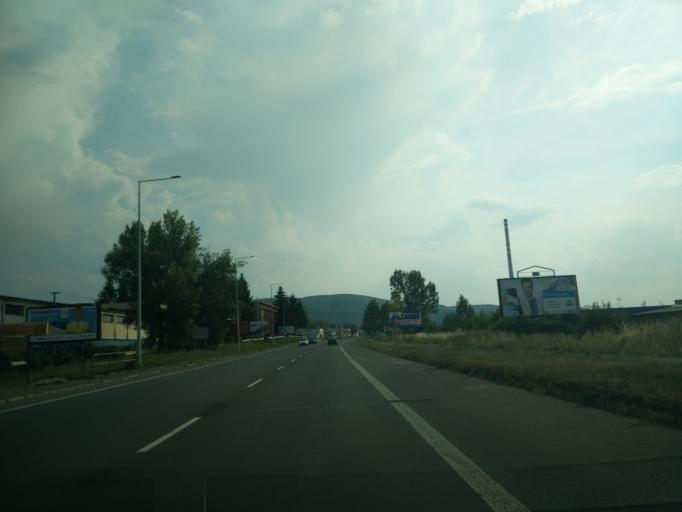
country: SK
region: Banskobystricky
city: Ziar nad Hronom
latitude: 48.5738
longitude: 18.8689
